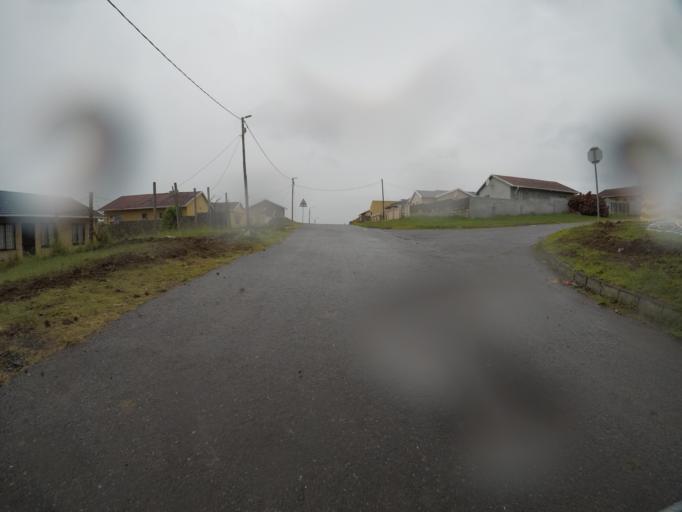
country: ZA
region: Eastern Cape
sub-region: Buffalo City Metropolitan Municipality
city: East London
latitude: -32.9950
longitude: 27.8419
